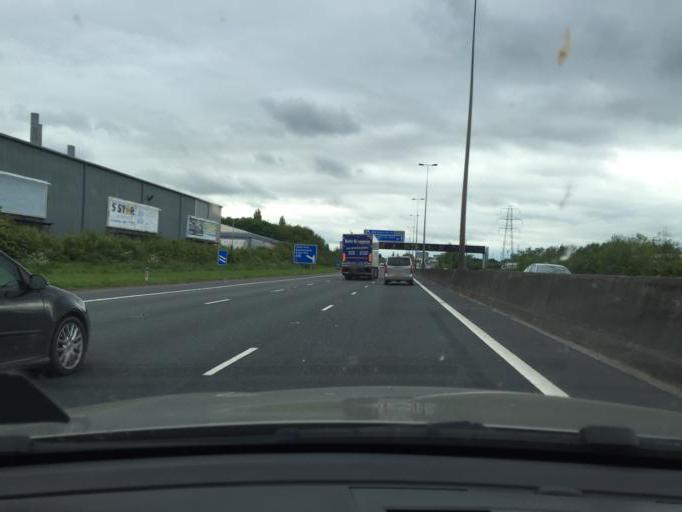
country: GB
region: Northern Ireland
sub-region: City of Belfast
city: Belfast
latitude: 54.5791
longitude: -5.9695
